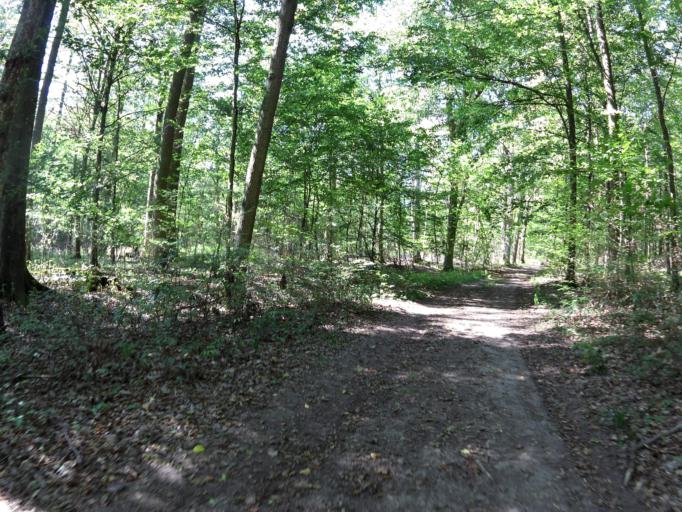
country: DE
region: Bavaria
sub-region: Regierungsbezirk Unterfranken
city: Gadheim
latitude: 49.8543
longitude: 9.8918
